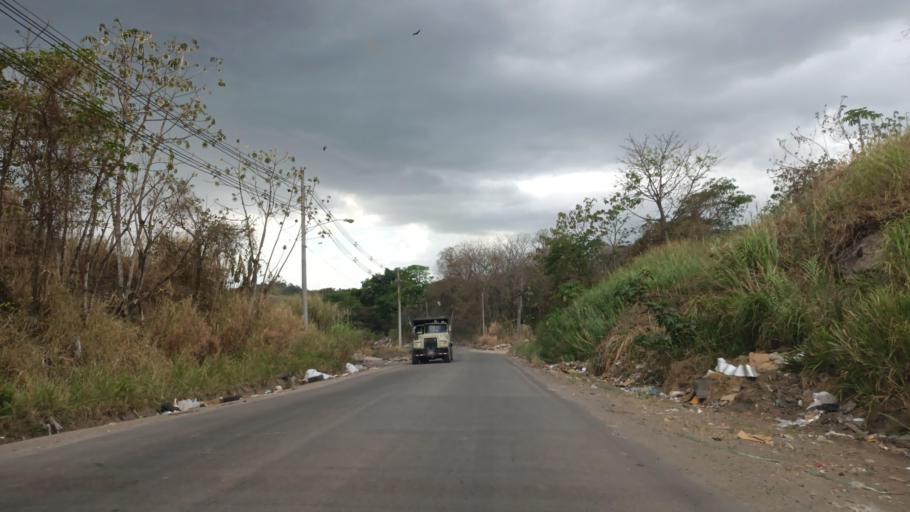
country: PA
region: Panama
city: Las Cumbres
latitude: 9.0504
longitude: -79.5635
